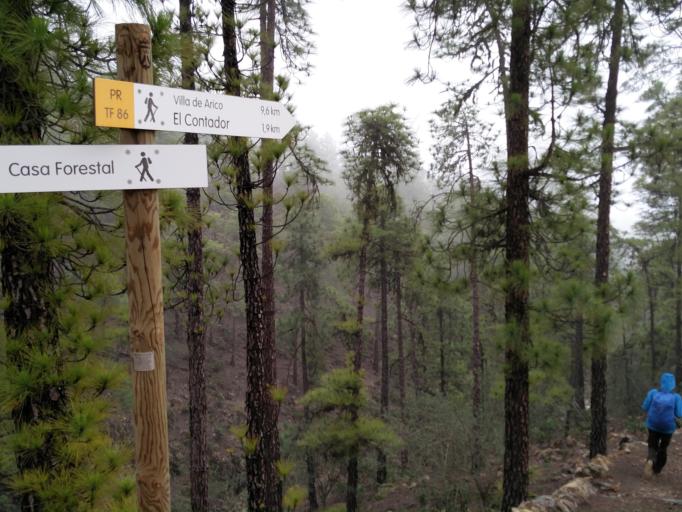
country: ES
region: Canary Islands
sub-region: Provincia de Santa Cruz de Tenerife
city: Lomo de Arico
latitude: 28.2067
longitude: -16.5504
